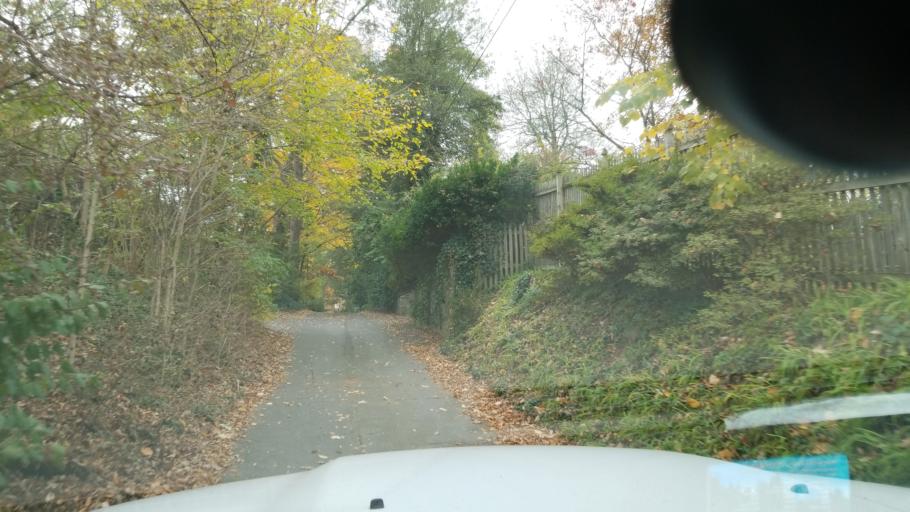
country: US
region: Maryland
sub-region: Montgomery County
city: Chevy Chase
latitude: 38.9488
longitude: -77.0603
